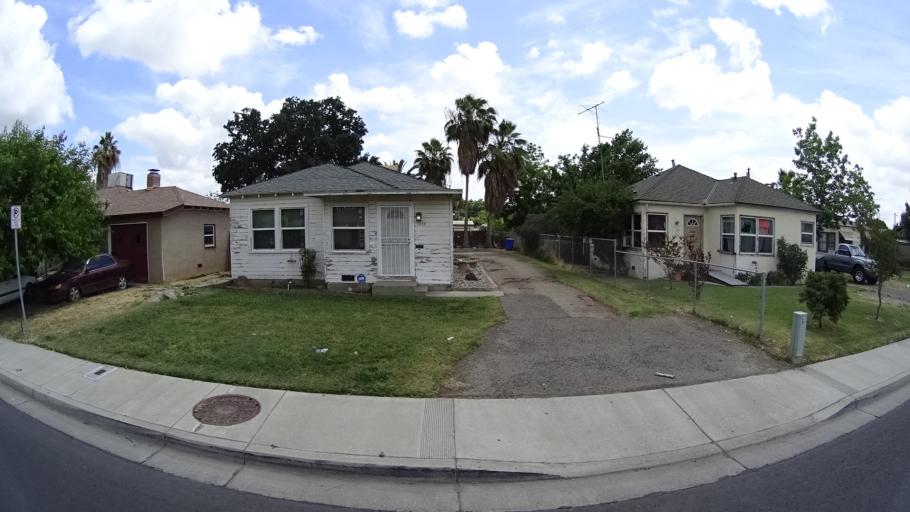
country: US
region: California
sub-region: Kings County
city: Hanford
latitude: 36.3382
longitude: -119.6551
